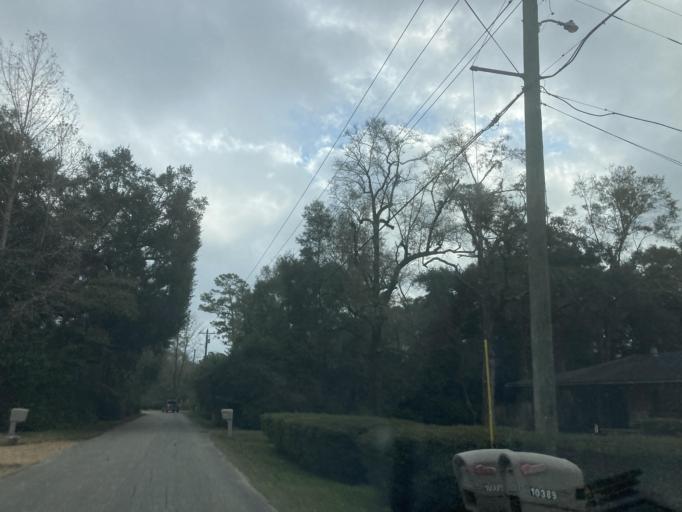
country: US
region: Mississippi
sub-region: Harrison County
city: West Gulfport
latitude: 30.4797
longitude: -89.0140
